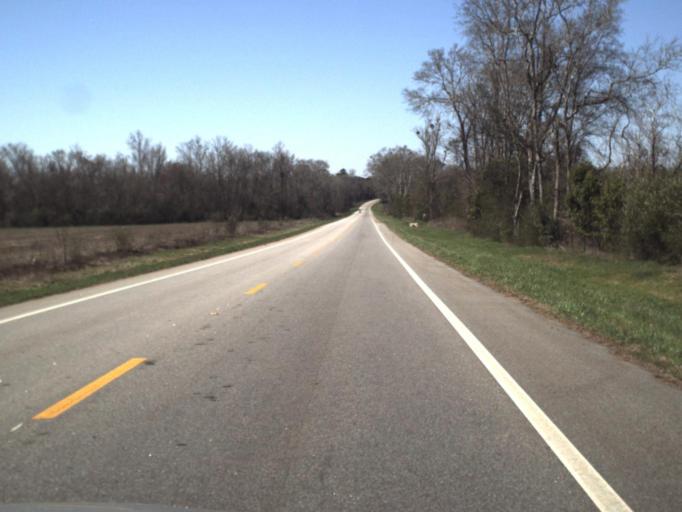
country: US
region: Florida
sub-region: Jackson County
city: Marianna
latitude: 30.8179
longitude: -85.3153
